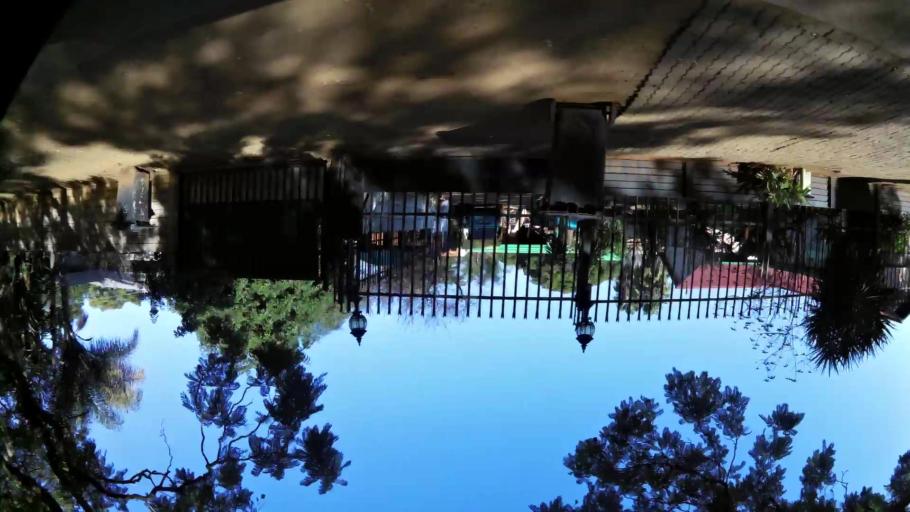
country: ZA
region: Gauteng
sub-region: City of Tshwane Metropolitan Municipality
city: Pretoria
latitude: -25.6660
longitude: 28.1706
